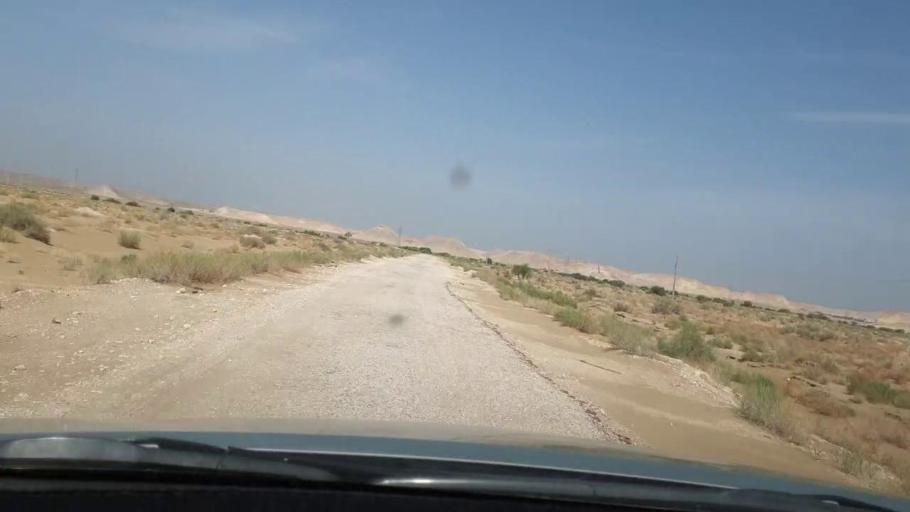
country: PK
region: Sindh
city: Kot Diji
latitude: 27.3277
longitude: 68.7978
